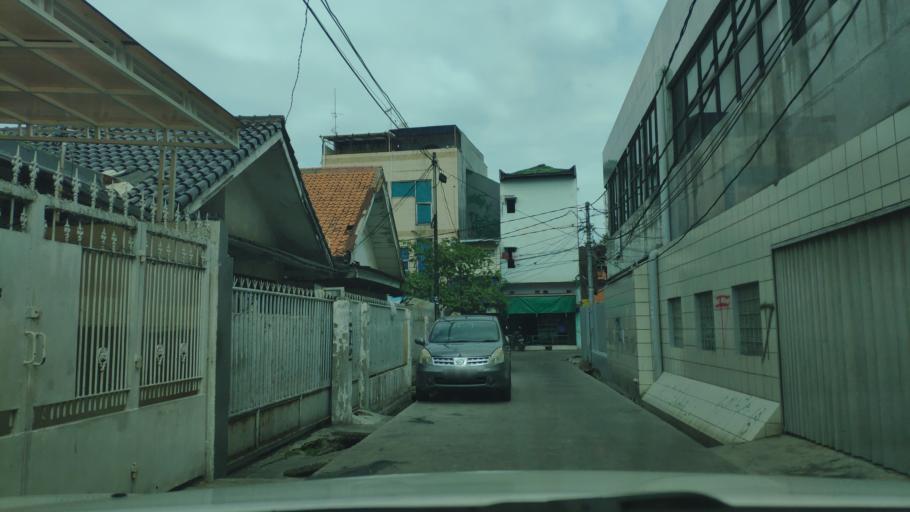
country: ID
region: Jakarta Raya
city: Jakarta
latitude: -6.1488
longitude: 106.8190
